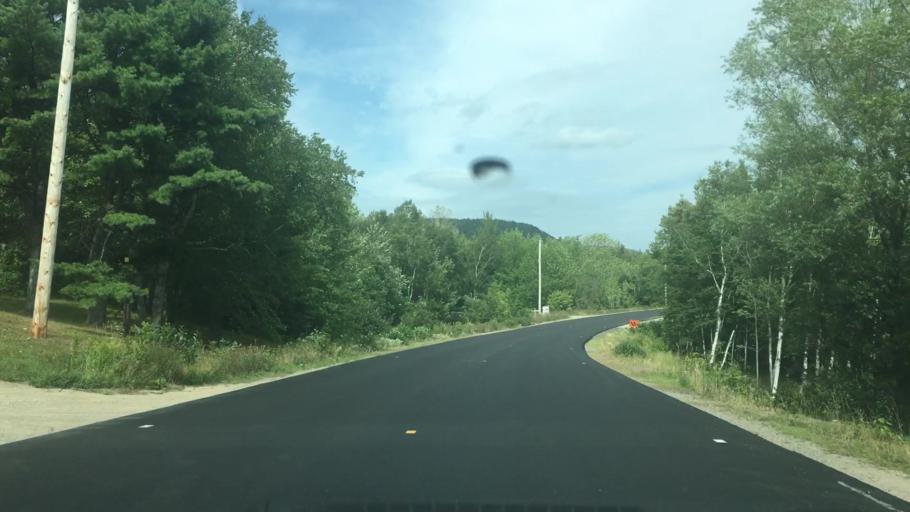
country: CA
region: Nova Scotia
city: Sydney Mines
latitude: 46.5494
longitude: -60.4118
